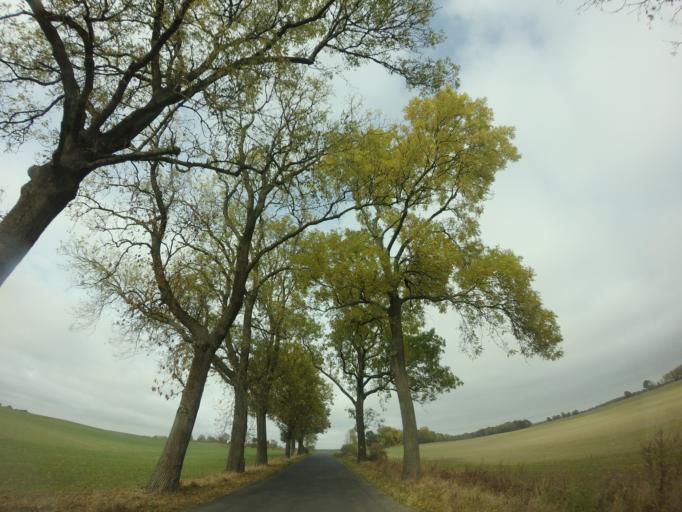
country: PL
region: West Pomeranian Voivodeship
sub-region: Powiat choszczenski
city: Recz
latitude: 53.2279
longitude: 15.6048
